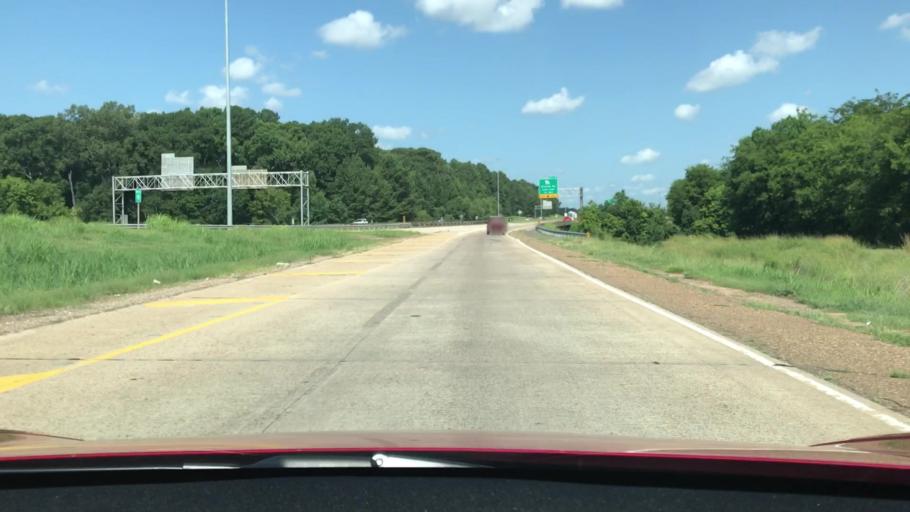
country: US
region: Louisiana
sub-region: Bossier Parish
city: Bossier City
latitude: 32.4126
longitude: -93.7267
